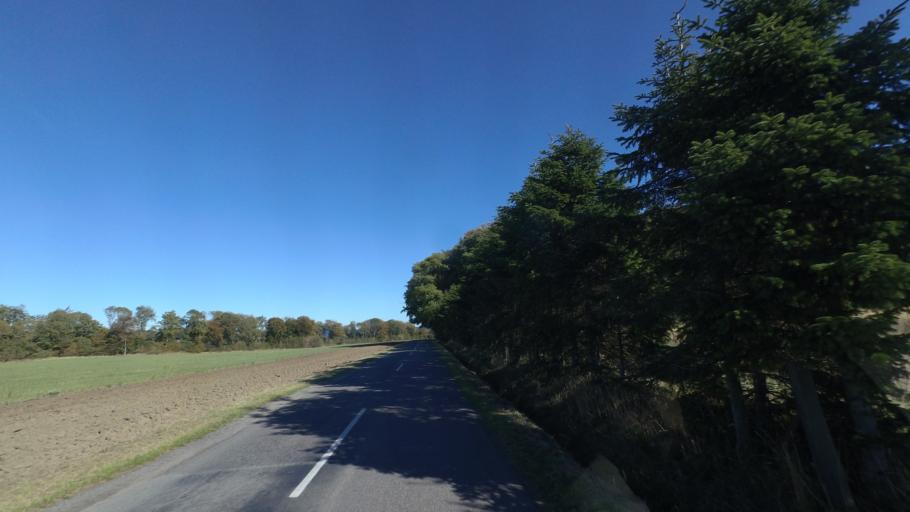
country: DK
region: Capital Region
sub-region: Bornholm Kommune
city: Nexo
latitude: 55.1107
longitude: 15.1215
